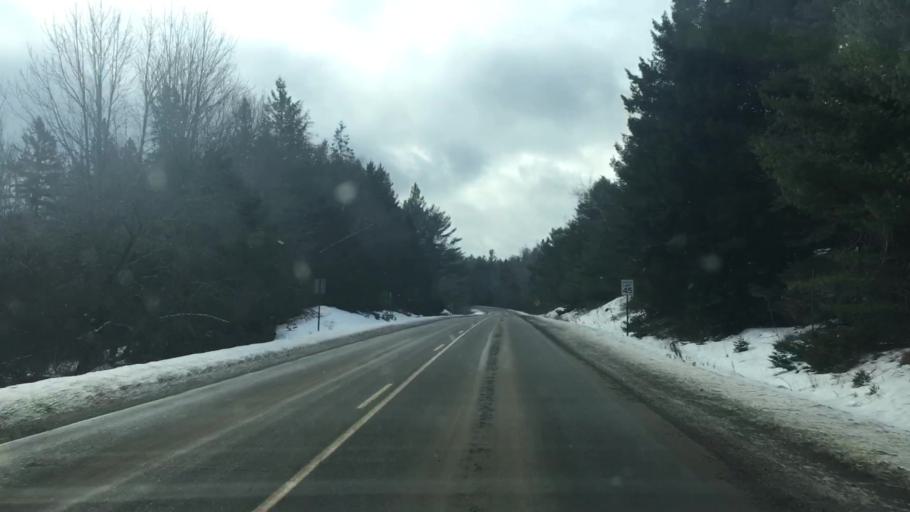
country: US
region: Maine
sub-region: Washington County
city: Calais
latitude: 45.0486
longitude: -67.3267
